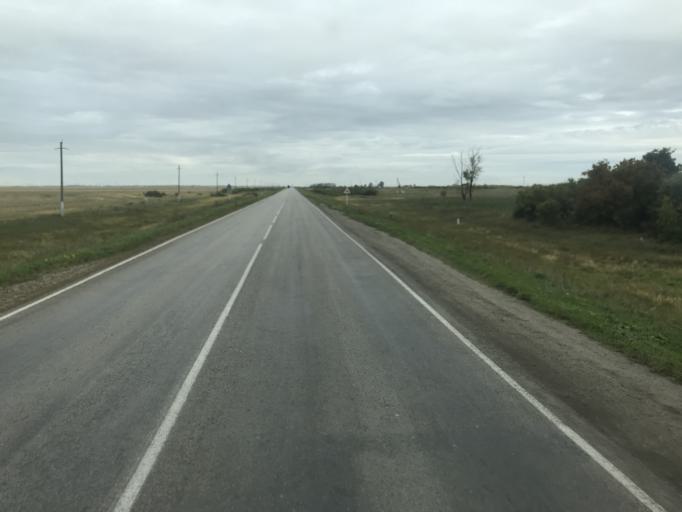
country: KZ
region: Qostanay
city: Komsomolets
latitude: 53.8760
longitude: 61.9580
